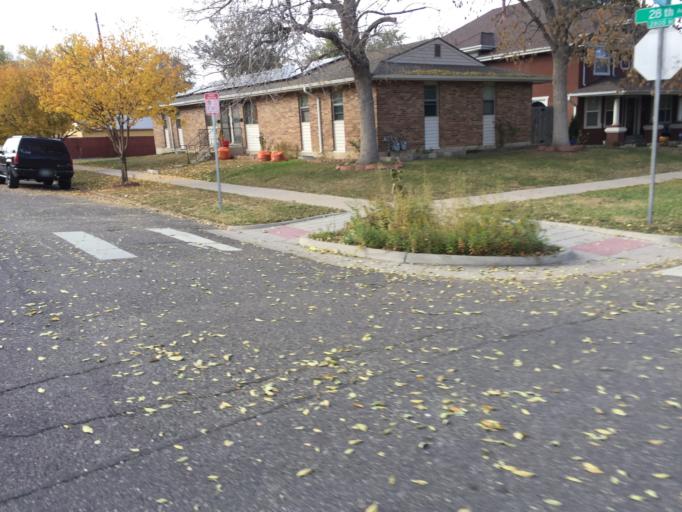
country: US
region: Colorado
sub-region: Denver County
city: Denver
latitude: 39.7570
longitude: -104.9696
